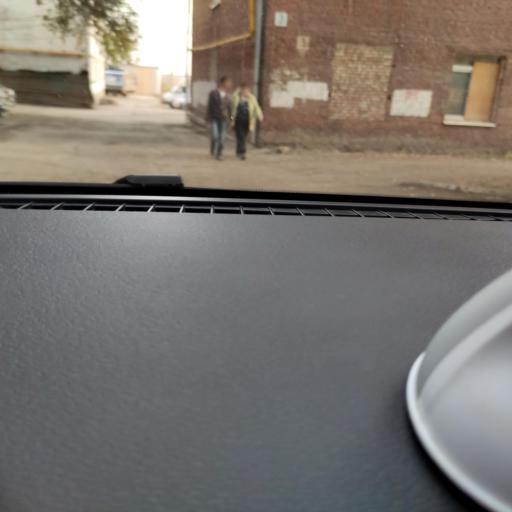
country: RU
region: Samara
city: Samara
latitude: 53.1715
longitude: 50.1911
